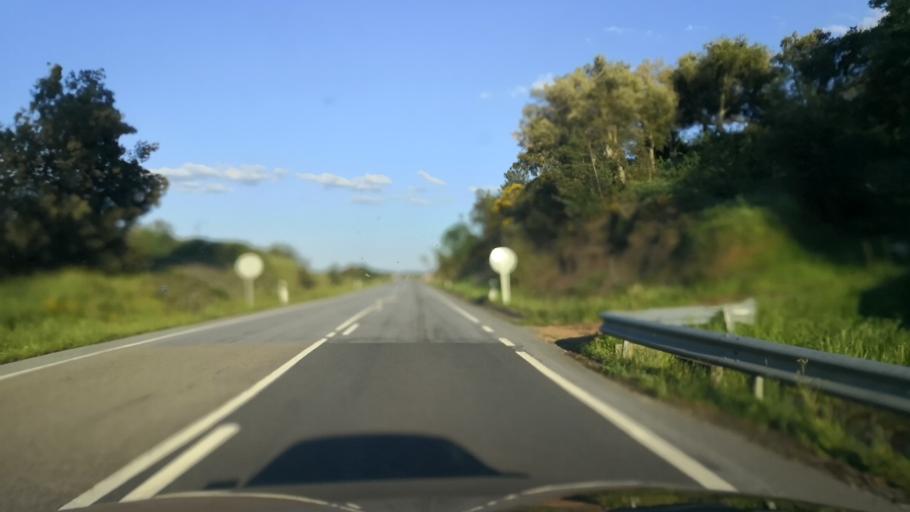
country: PT
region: Portalegre
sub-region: Marvao
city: Marvao
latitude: 39.3802
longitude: -7.3746
